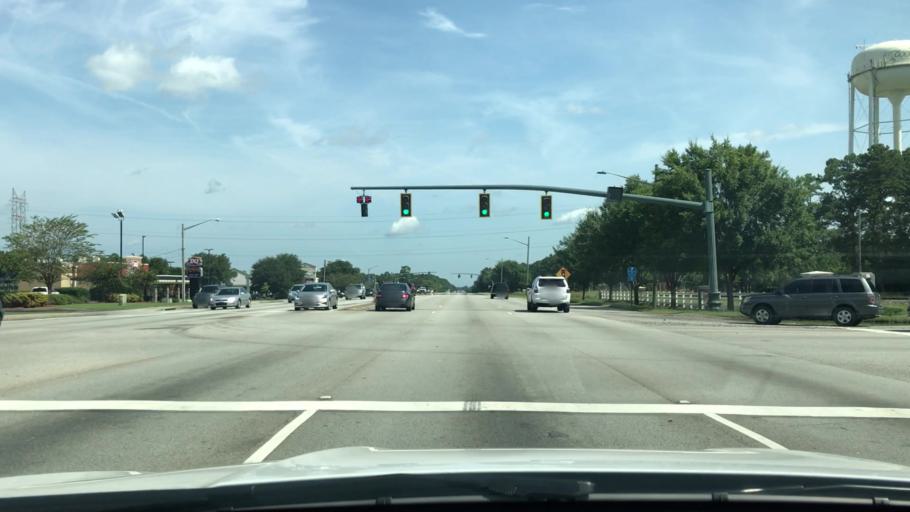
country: US
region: South Carolina
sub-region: Berkeley County
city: Goose Creek
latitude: 33.0011
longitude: -80.0381
